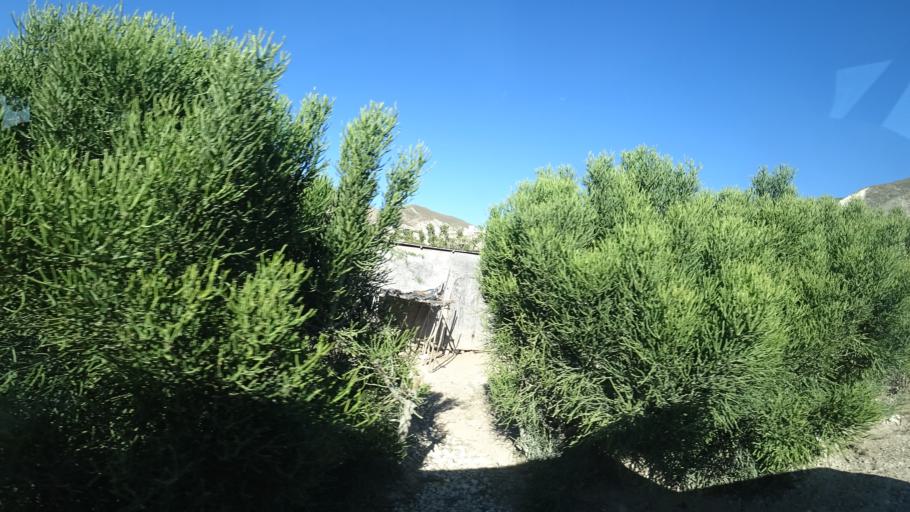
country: HT
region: Ouest
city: Croix des Bouquets
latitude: 18.6775
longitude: -72.2408
